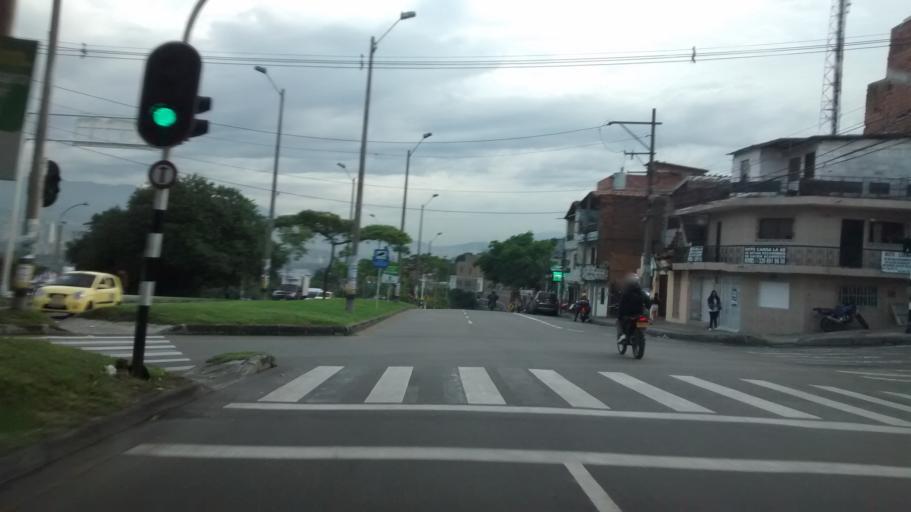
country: CO
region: Antioquia
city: Medellin
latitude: 6.2907
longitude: -75.5698
